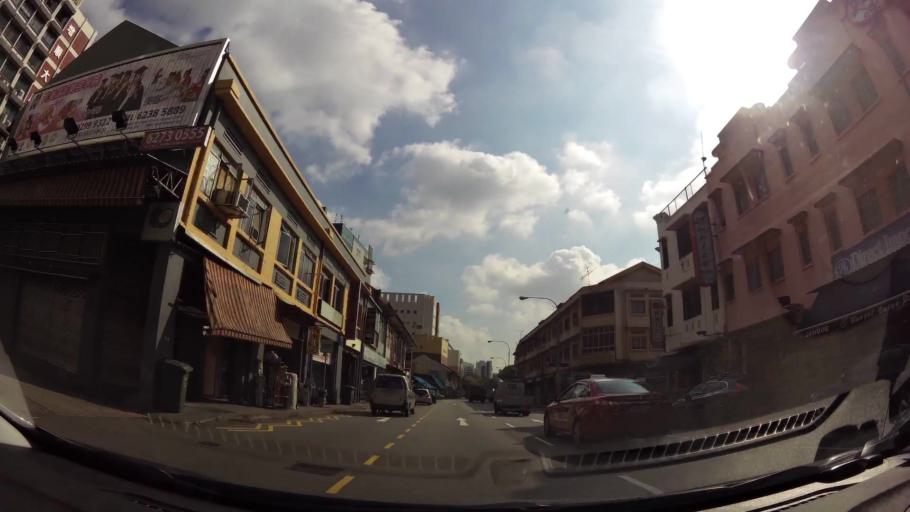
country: SG
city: Singapore
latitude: 1.3141
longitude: 103.8777
